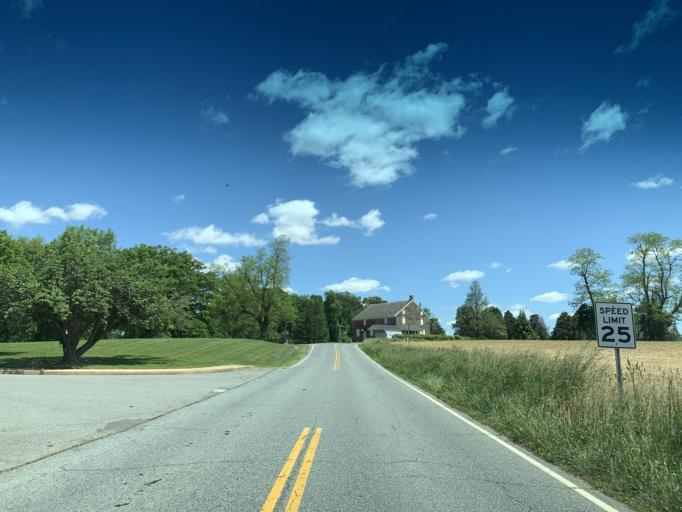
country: US
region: Maryland
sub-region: Cecil County
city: Rising Sun
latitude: 39.6997
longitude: -75.9836
